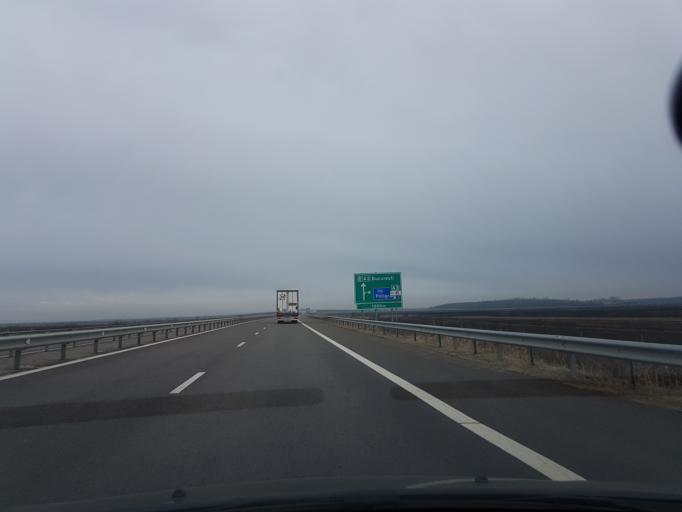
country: RO
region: Prahova
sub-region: Comuna Olari
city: Olari
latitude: 44.7894
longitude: 26.2412
